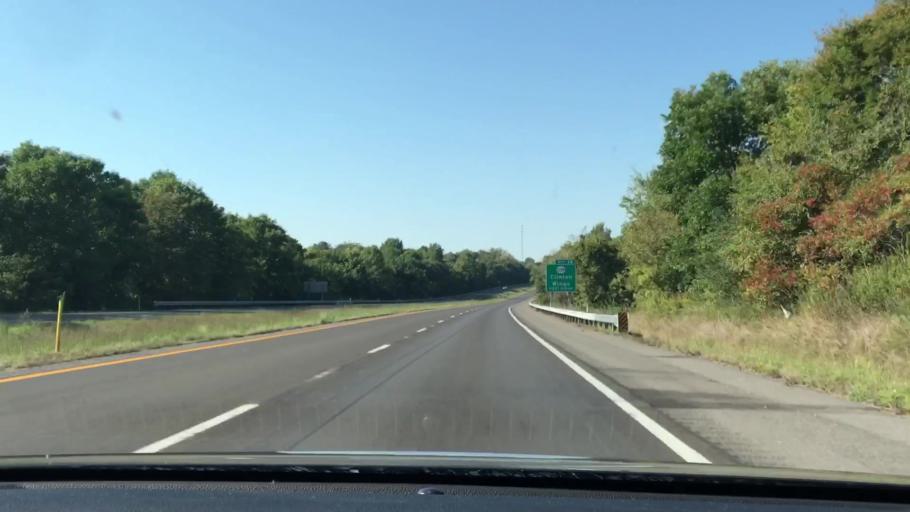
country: US
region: Kentucky
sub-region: Graves County
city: Mayfield
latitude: 36.6531
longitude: -88.7463
